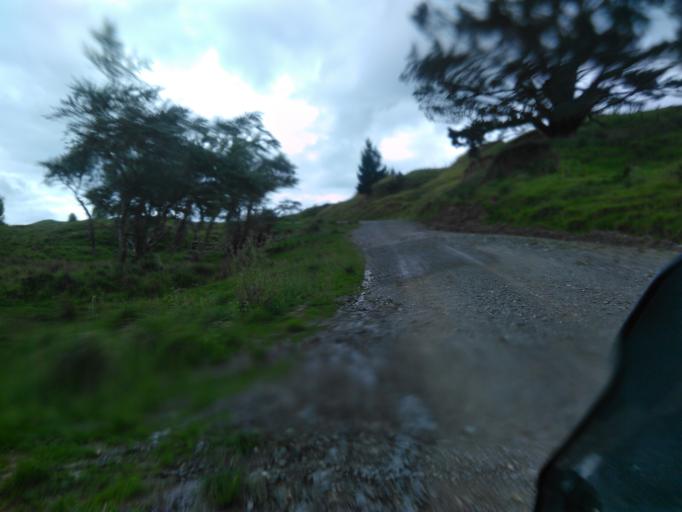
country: NZ
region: Gisborne
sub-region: Gisborne District
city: Gisborne
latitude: -38.0698
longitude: 178.0458
